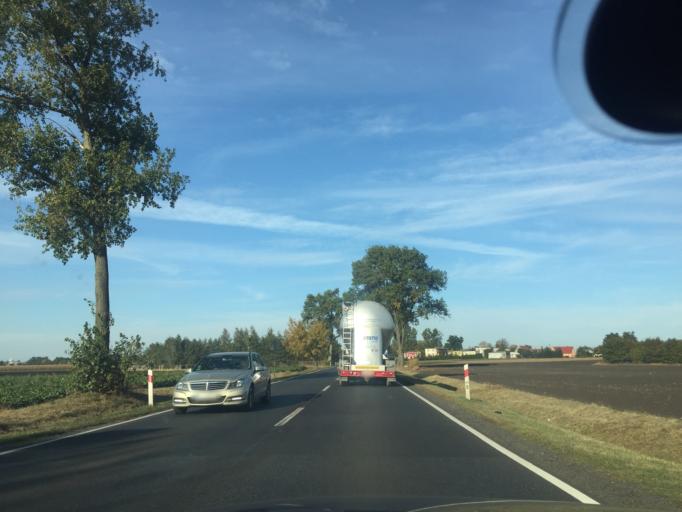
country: PL
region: Kujawsko-Pomorskie
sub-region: Powiat inowroclawski
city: Inowroclaw
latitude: 52.7276
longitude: 18.2316
